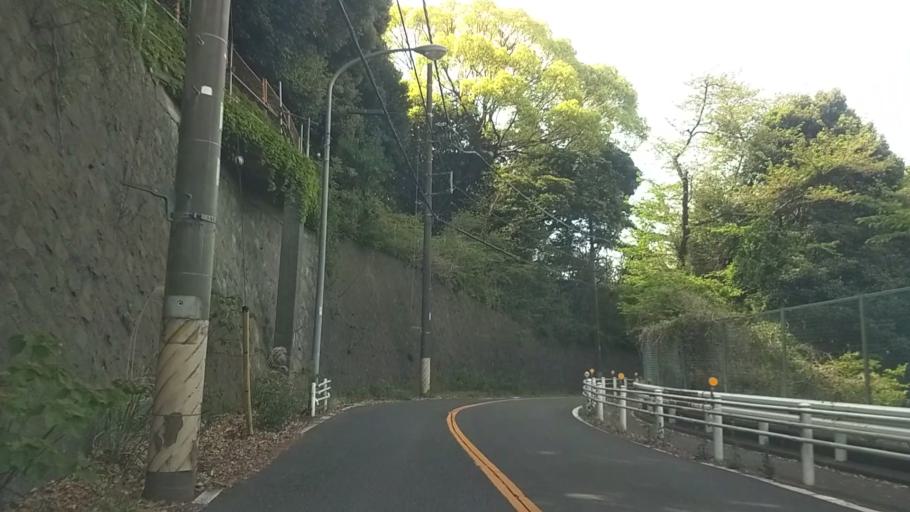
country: JP
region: Kanagawa
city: Yokohama
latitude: 35.3702
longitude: 139.6296
